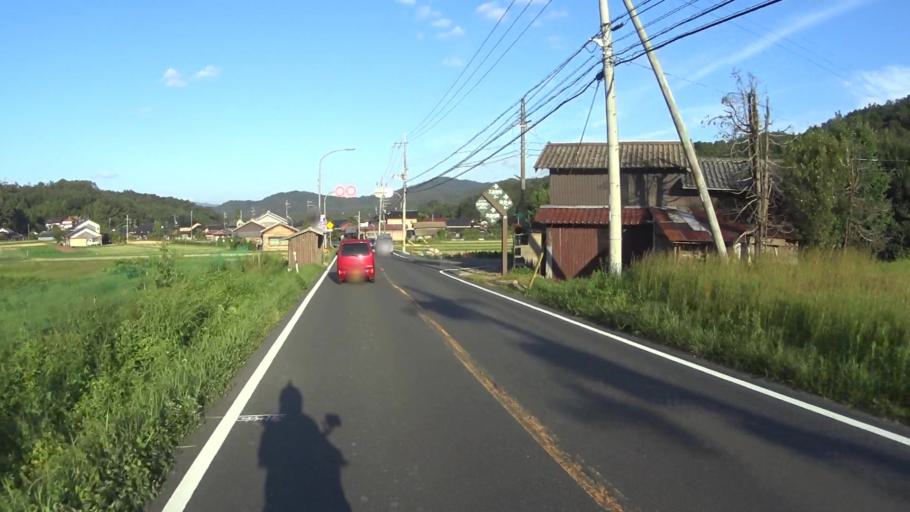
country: JP
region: Kyoto
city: Miyazu
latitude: 35.5783
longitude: 135.0187
